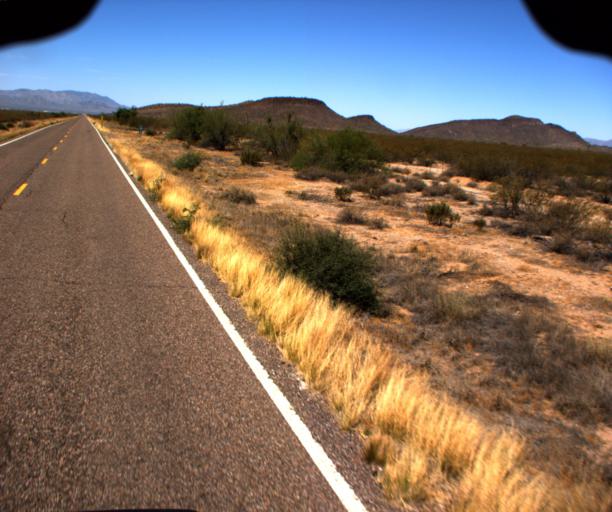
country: US
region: Arizona
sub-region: Yavapai County
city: Congress
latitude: 34.0223
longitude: -113.0938
